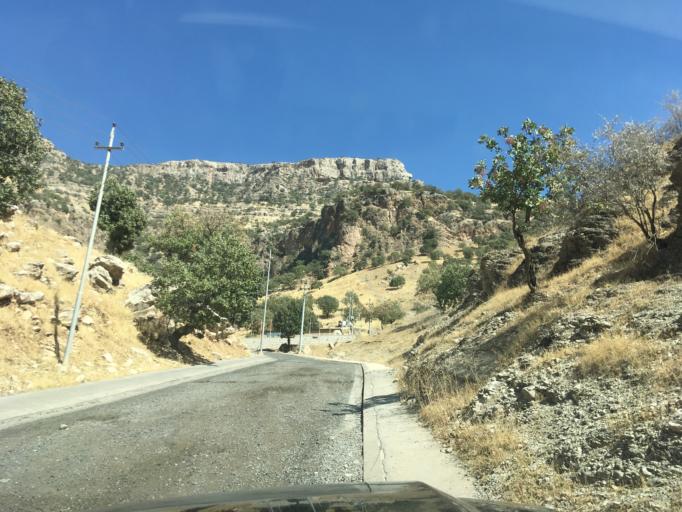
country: IQ
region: Arbil
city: Mergasur
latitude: 36.8317
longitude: 44.2167
